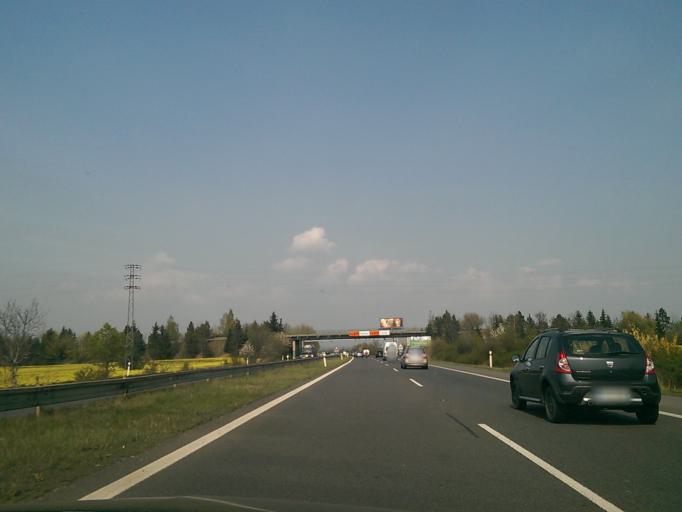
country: CZ
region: Central Bohemia
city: Zelenec
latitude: 50.1425
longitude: 14.6493
